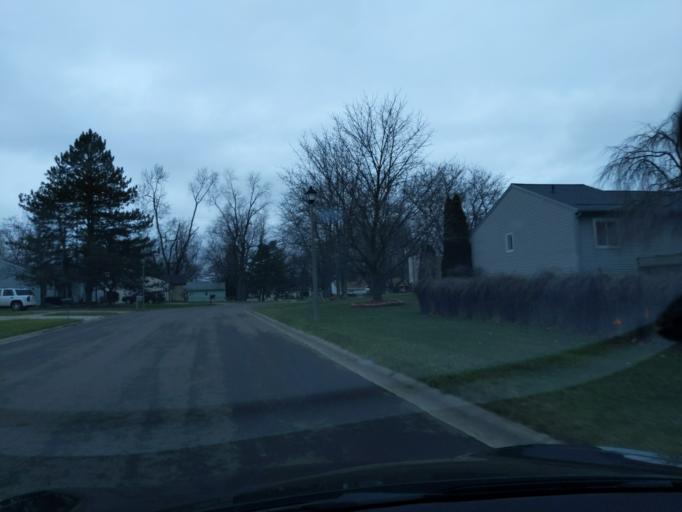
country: US
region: Michigan
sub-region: Eaton County
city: Waverly
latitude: 42.7362
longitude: -84.6115
